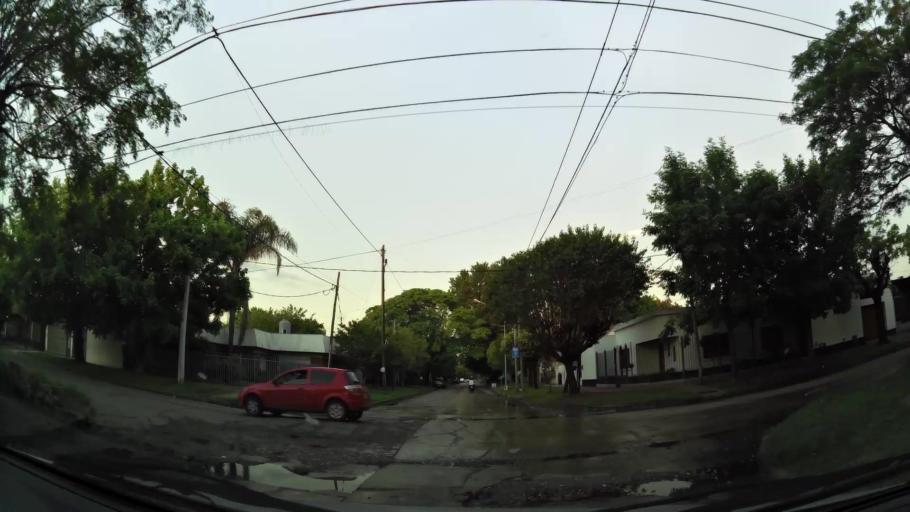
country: AR
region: Buenos Aires
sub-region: Partido de Lomas de Zamora
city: Lomas de Zamora
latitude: -34.7662
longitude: -58.3750
